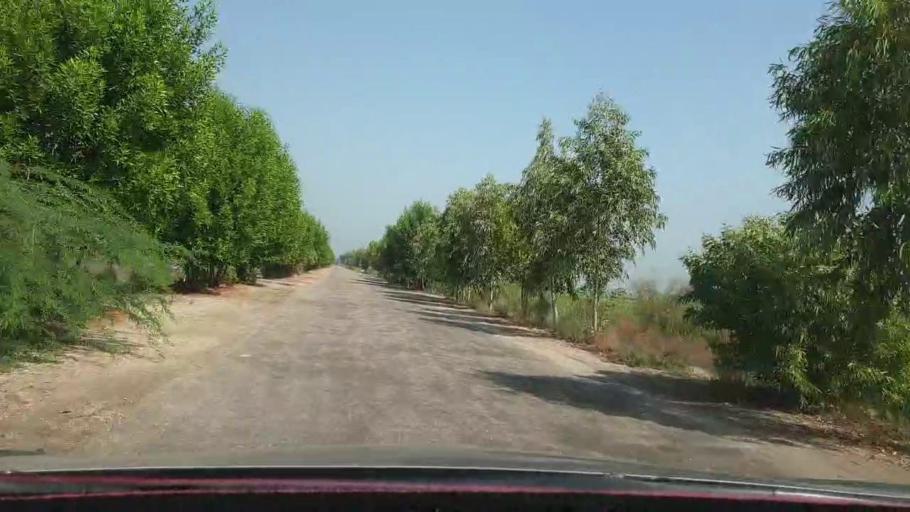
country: PK
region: Sindh
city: Warah
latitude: 27.4663
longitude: 67.8341
